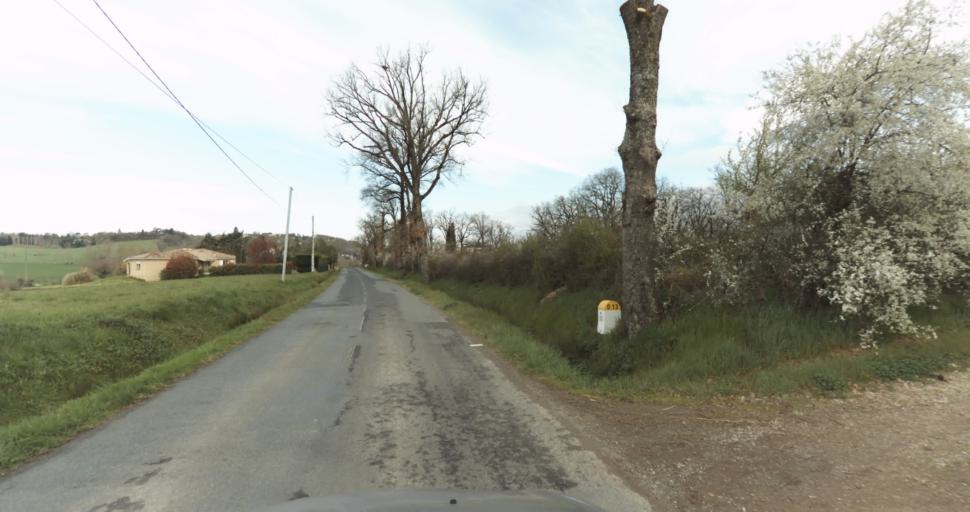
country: FR
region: Midi-Pyrenees
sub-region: Departement du Tarn
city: Puygouzon
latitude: 43.8908
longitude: 2.1919
